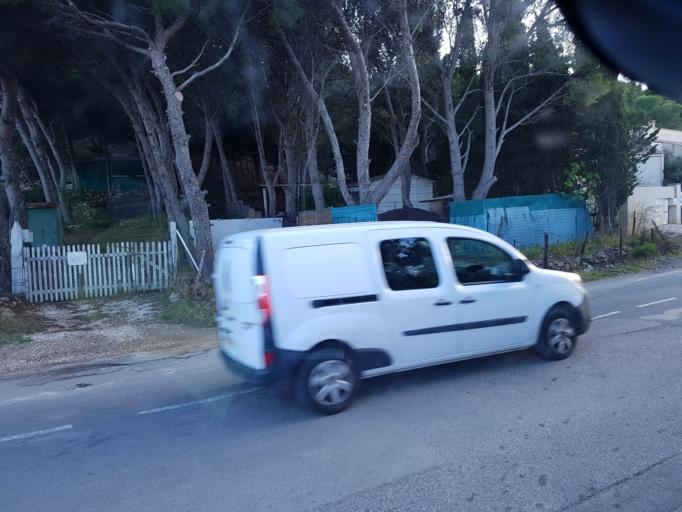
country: FR
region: Languedoc-Roussillon
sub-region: Departement de l'Aude
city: Leucate
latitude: 42.9347
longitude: 3.0264
